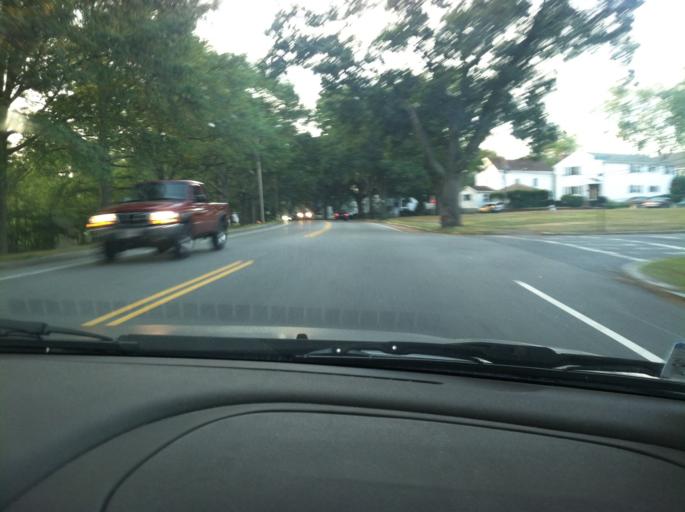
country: US
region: Massachusetts
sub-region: Middlesex County
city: Arlington
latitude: 42.4218
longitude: -71.1443
